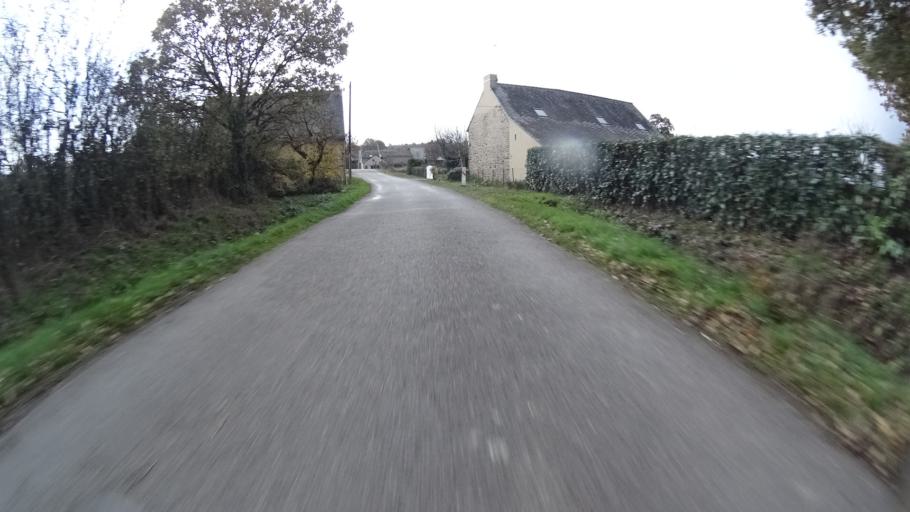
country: FR
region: Pays de la Loire
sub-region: Departement de la Loire-Atlantique
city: Avessac
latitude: 47.6627
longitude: -2.0252
